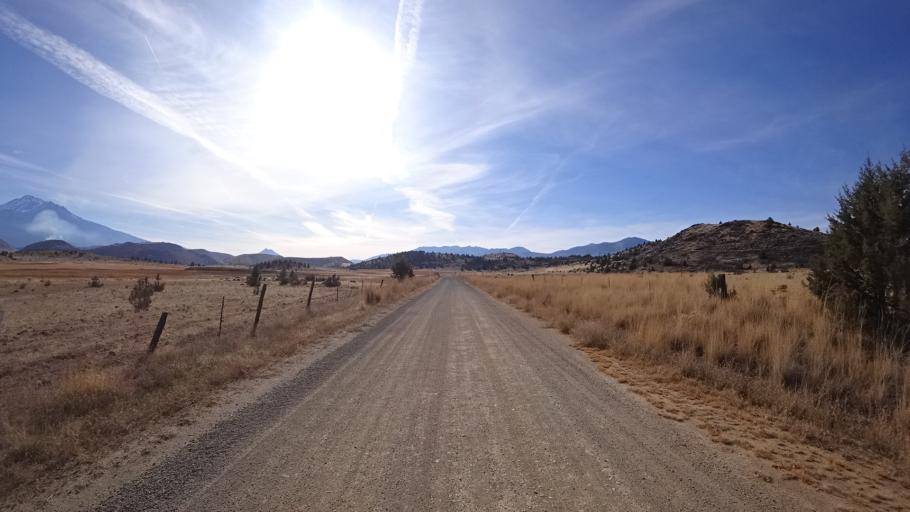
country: US
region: California
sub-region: Siskiyou County
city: Weed
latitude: 41.5459
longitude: -122.4726
